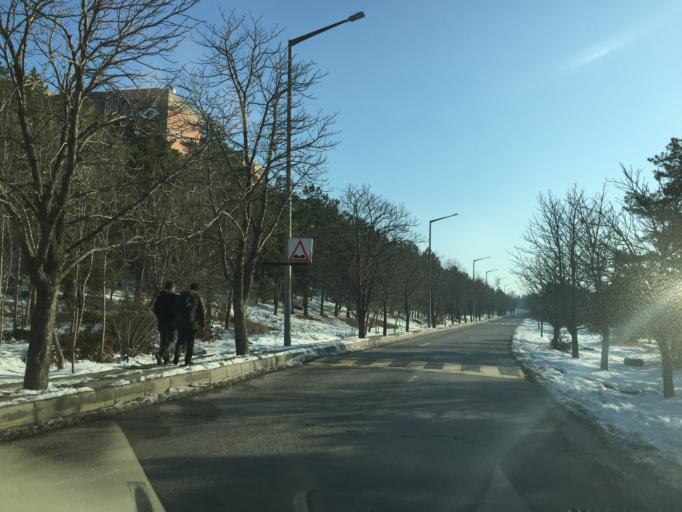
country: TR
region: Ankara
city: Ankara
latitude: 39.8951
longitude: 32.7809
